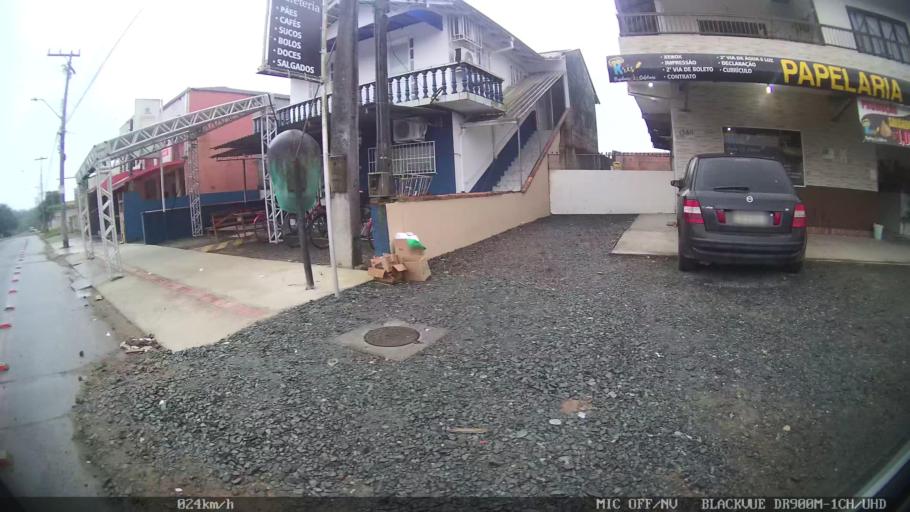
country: BR
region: Santa Catarina
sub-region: Joinville
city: Joinville
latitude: -26.2061
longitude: -48.8300
